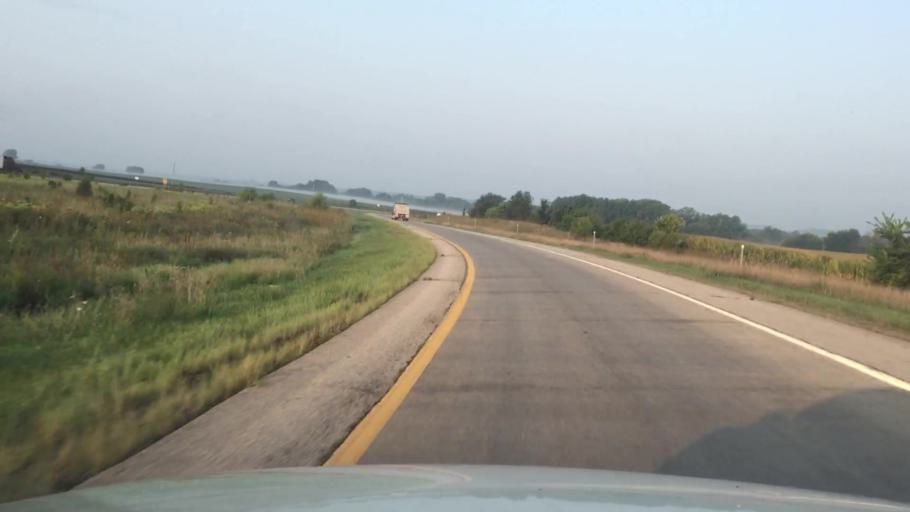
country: US
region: Iowa
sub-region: Polk County
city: Altoona
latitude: 41.6609
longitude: -93.5274
